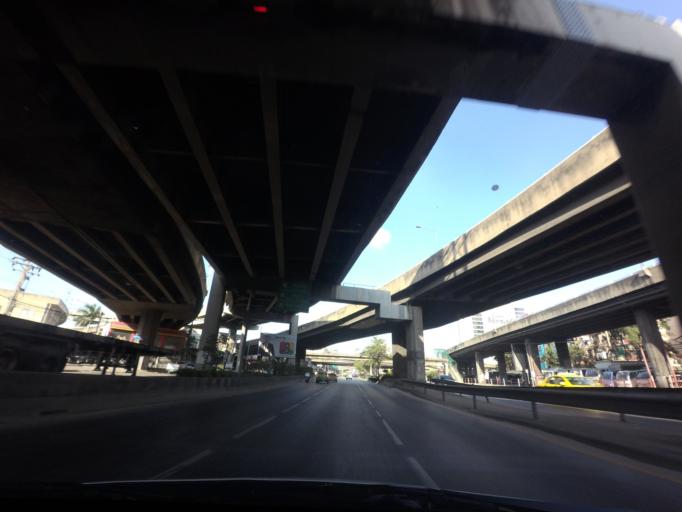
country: TH
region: Bangkok
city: Khlong Toei
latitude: 13.7151
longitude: 100.5557
